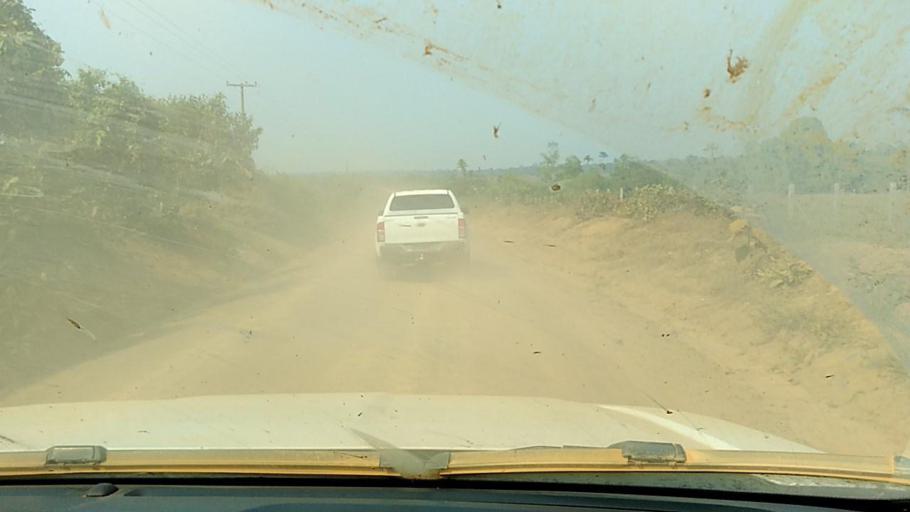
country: BR
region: Rondonia
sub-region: Porto Velho
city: Porto Velho
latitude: -8.8573
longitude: -64.1745
